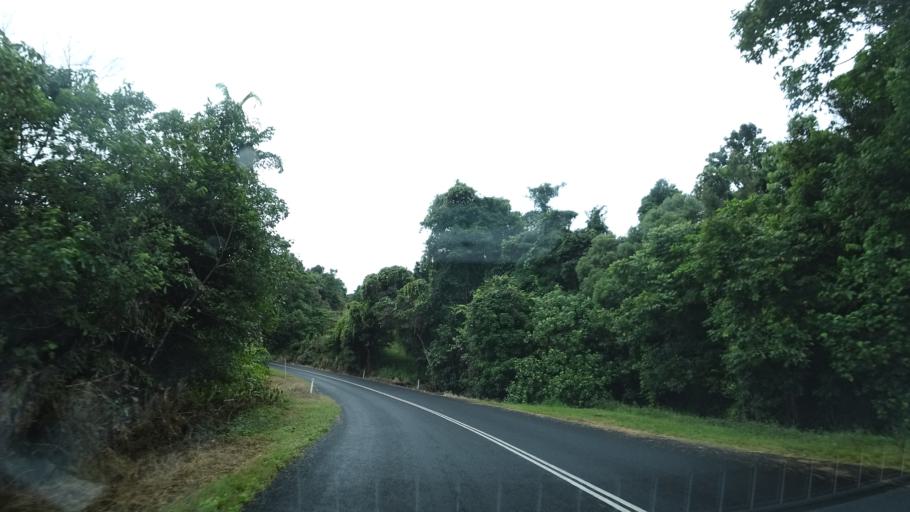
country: AU
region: Queensland
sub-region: Cassowary Coast
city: Innisfail
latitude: -17.5647
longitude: 146.0867
